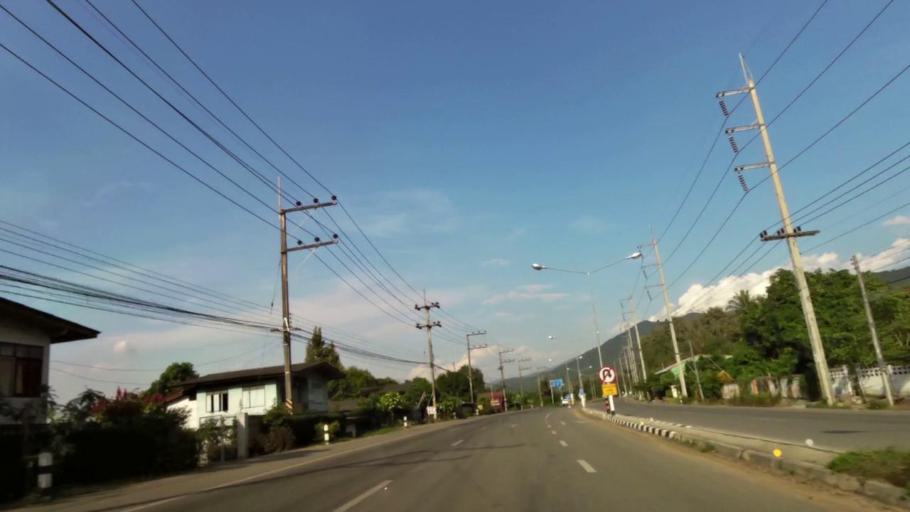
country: TH
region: Chiang Rai
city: Khun Tan
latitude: 19.8781
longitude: 100.2894
